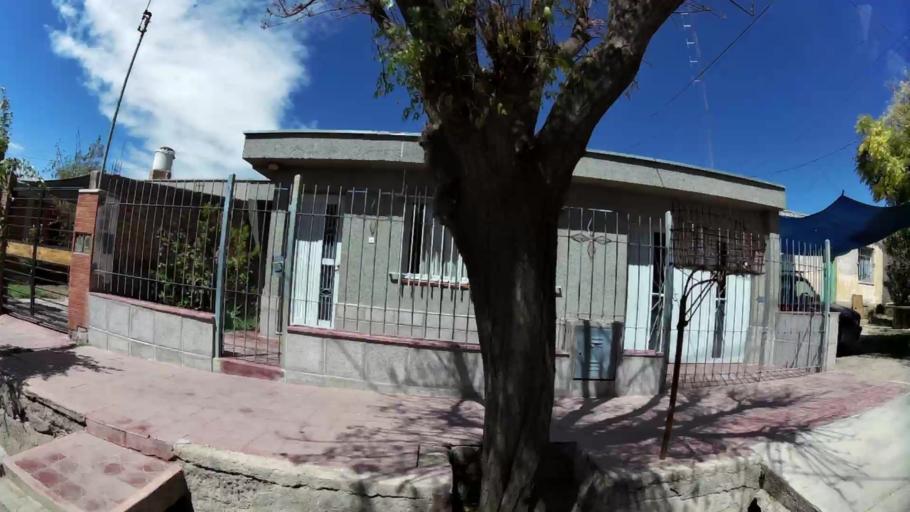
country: AR
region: Mendoza
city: Las Heras
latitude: -32.8633
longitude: -68.8666
